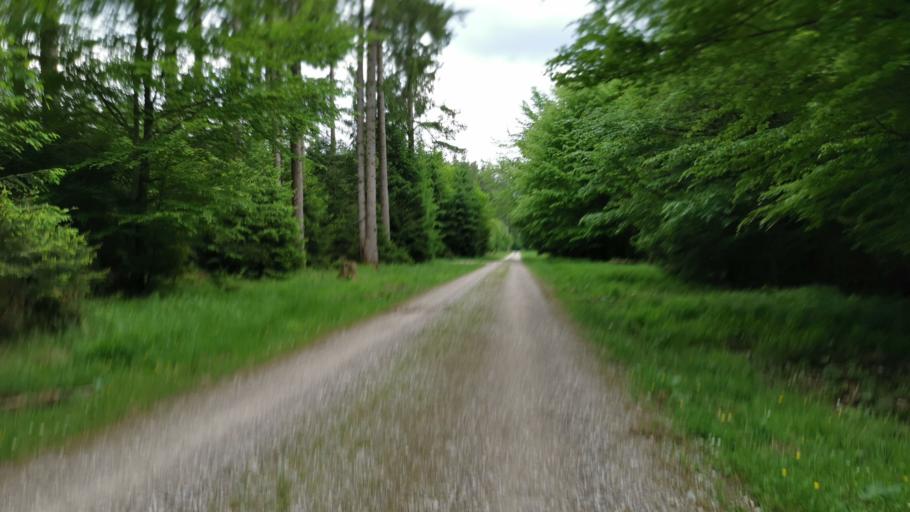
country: DE
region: Bavaria
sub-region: Upper Bavaria
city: Baierbrunn
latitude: 48.0414
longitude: 11.4748
